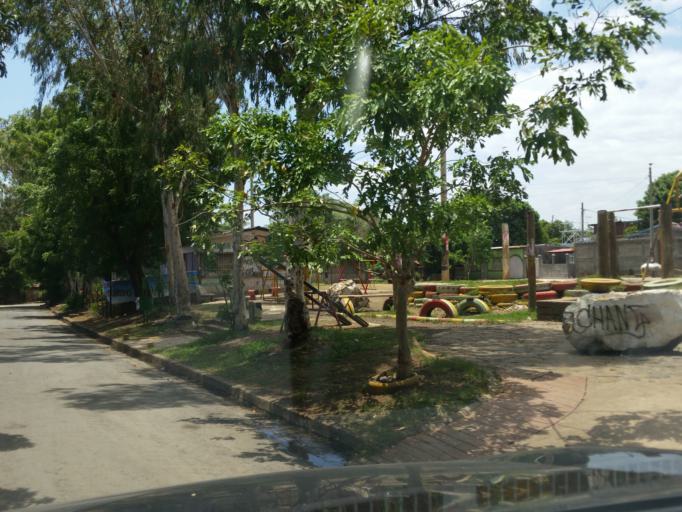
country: NI
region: Managua
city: Managua
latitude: 12.1182
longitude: -86.2440
